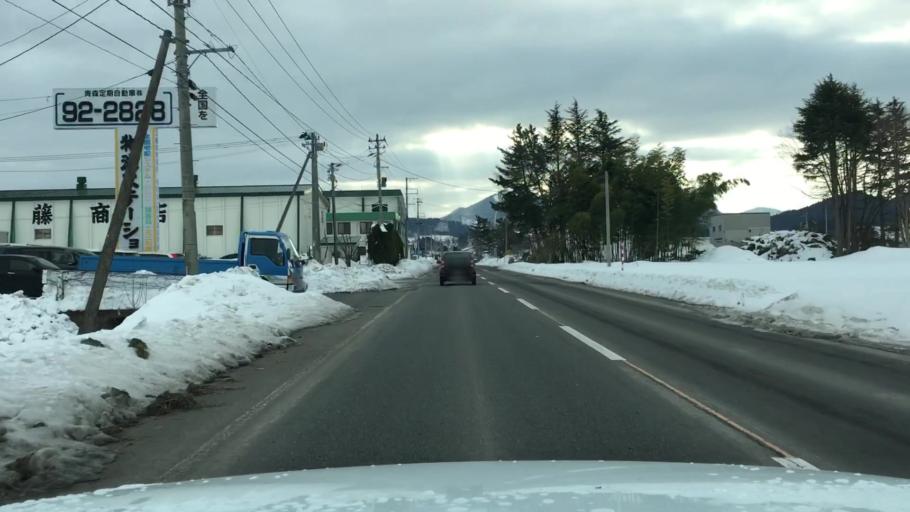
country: JP
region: Aomori
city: Hirosaki
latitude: 40.5603
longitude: 140.5319
